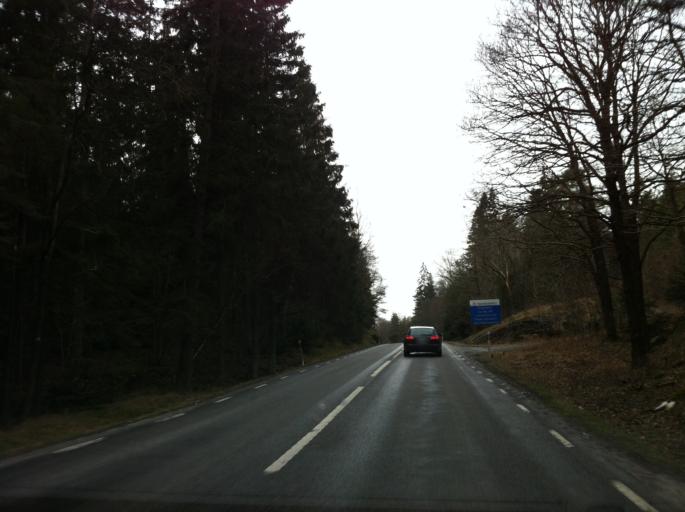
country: SE
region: Vaestra Goetaland
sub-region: Orust
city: Henan
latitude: 58.3122
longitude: 11.6924
